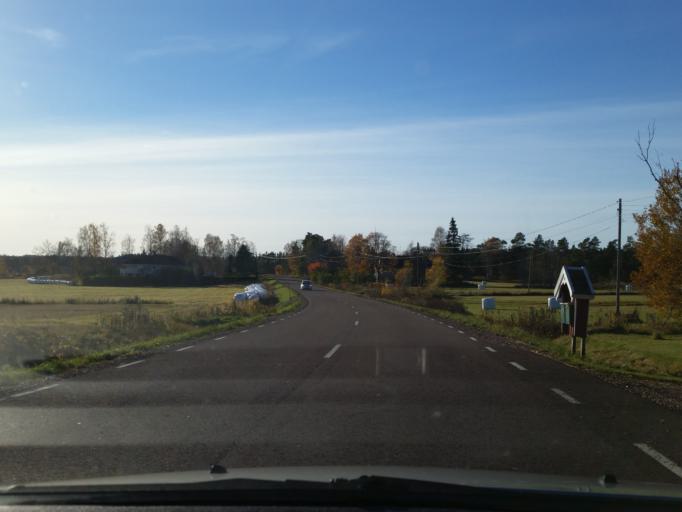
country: AX
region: Alands landsbygd
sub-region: Jomala
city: Jomala
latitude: 60.2107
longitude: 19.9676
